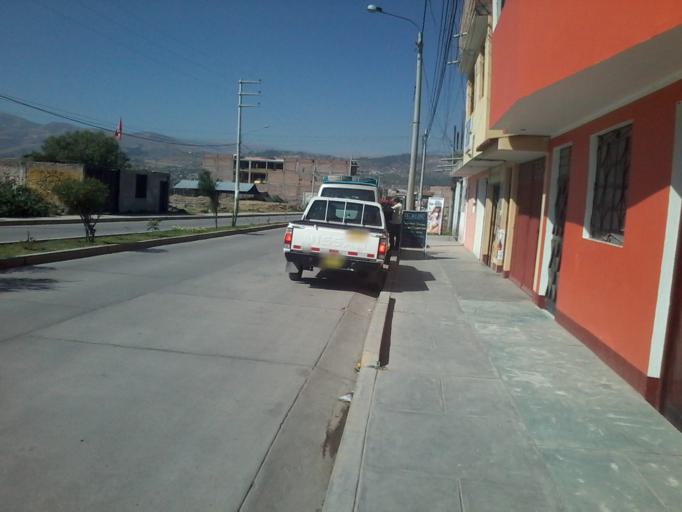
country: PE
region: Ayacucho
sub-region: Provincia de Huamanga
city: Ayacucho
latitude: -13.1556
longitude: -74.2074
